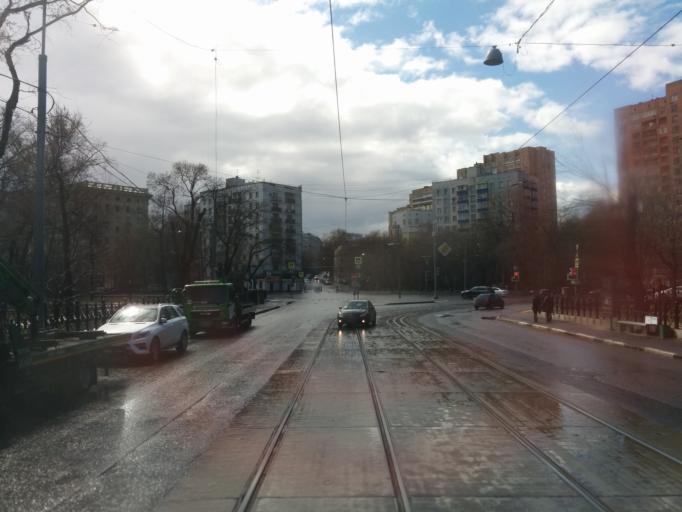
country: RU
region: Moscow
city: Mar'ina Roshcha
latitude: 55.7789
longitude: 37.6188
